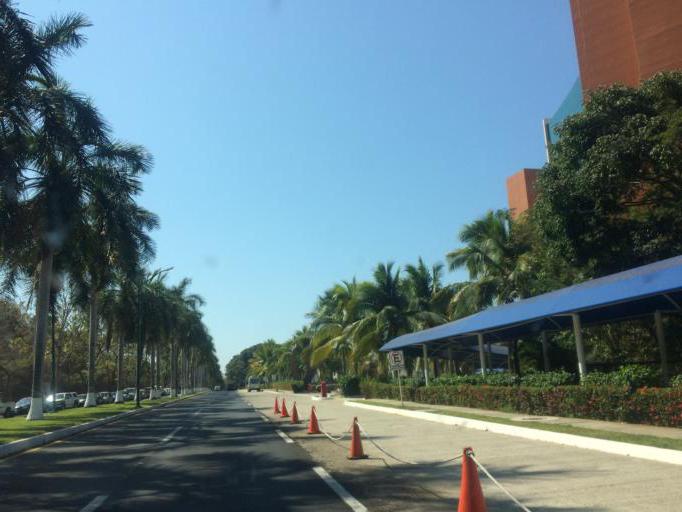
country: MX
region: Guerrero
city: Ixtapa
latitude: 17.6758
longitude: -101.6411
